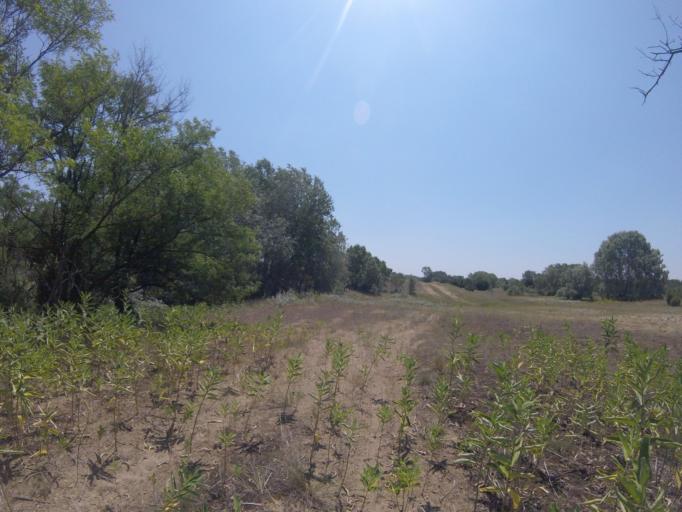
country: HU
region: Bacs-Kiskun
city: Jaszszentlaszlo
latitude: 46.6188
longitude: 19.7093
